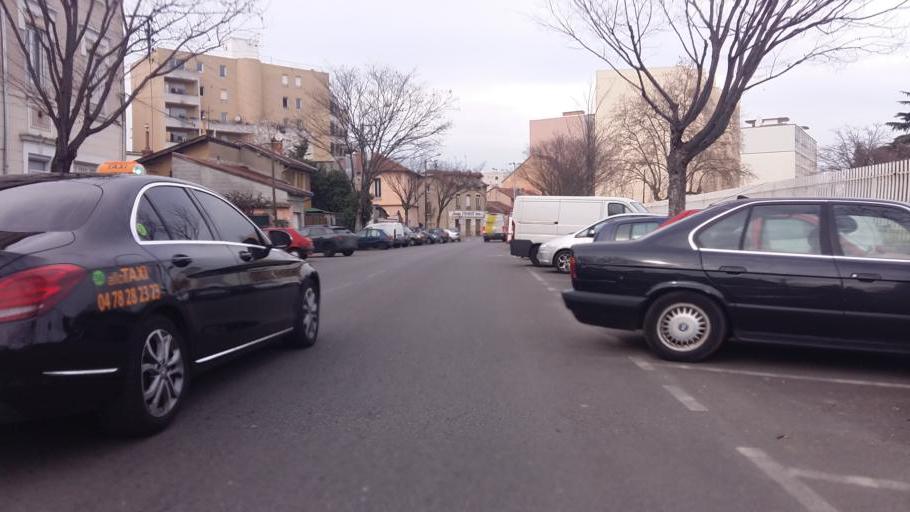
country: FR
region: Rhone-Alpes
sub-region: Departement du Rhone
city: Villeurbanne
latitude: 45.7622
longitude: 4.9005
